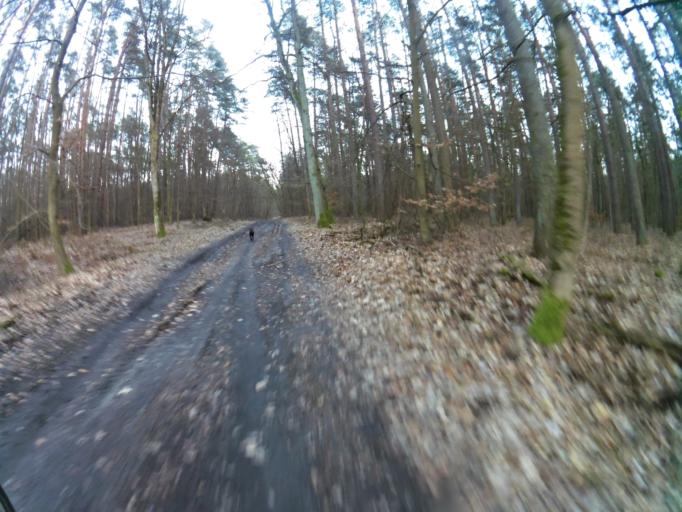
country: PL
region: West Pomeranian Voivodeship
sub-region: Powiat mysliborski
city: Debno
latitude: 52.8060
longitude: 14.8040
